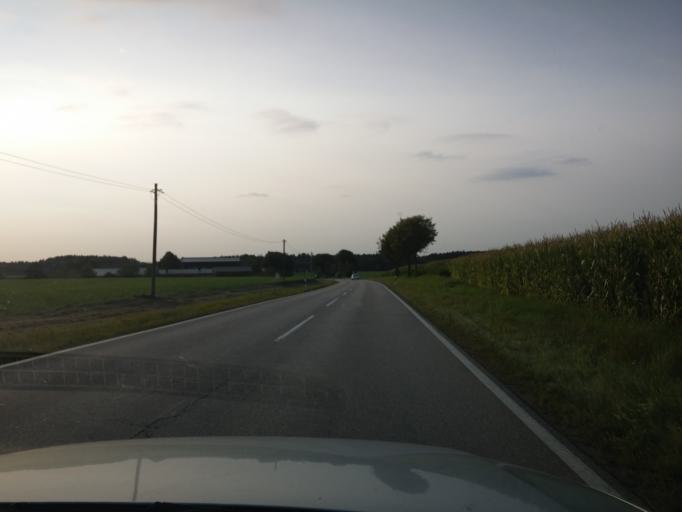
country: DE
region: Bavaria
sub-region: Upper Bavaria
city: Oberpframmern
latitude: 48.0245
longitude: 11.8056
